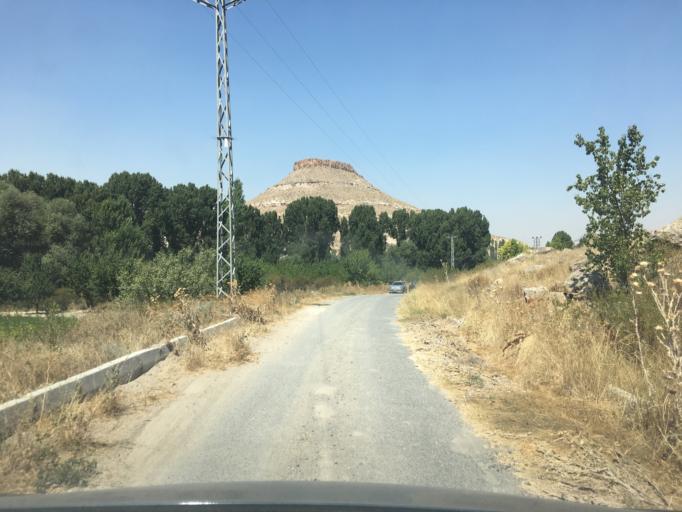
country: TR
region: Kayseri
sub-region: Yesilhisar
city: Yesilhisar
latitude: 38.4658
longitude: 34.9646
